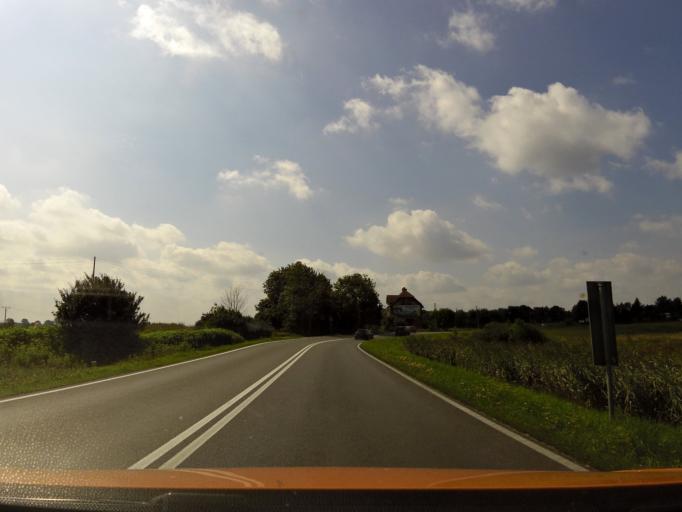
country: PL
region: West Pomeranian Voivodeship
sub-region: Powiat goleniowski
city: Nowogard
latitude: 53.7248
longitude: 15.1958
